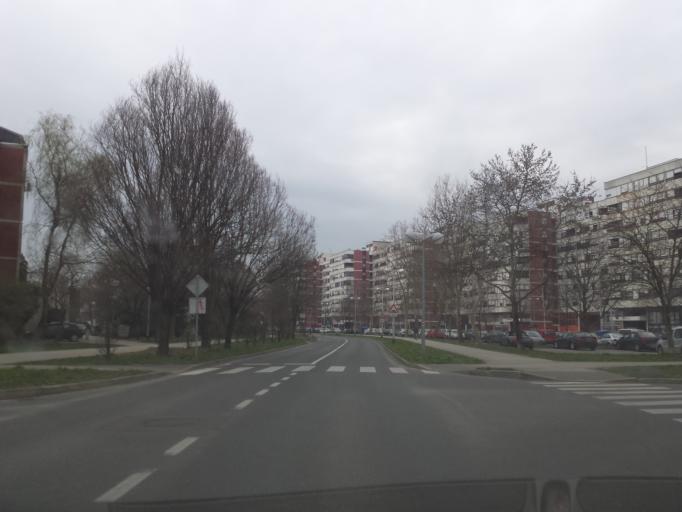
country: HR
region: Grad Zagreb
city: Jankomir
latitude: 45.8059
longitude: 15.8975
